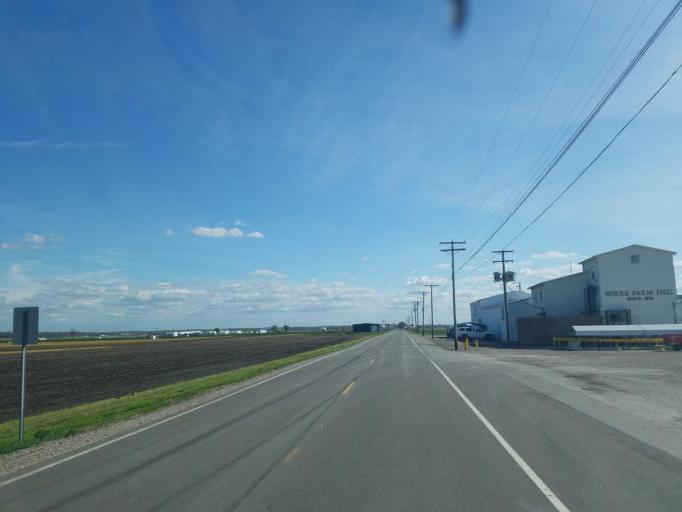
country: US
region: Ohio
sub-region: Huron County
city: Willard
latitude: 41.0238
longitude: -82.7316
